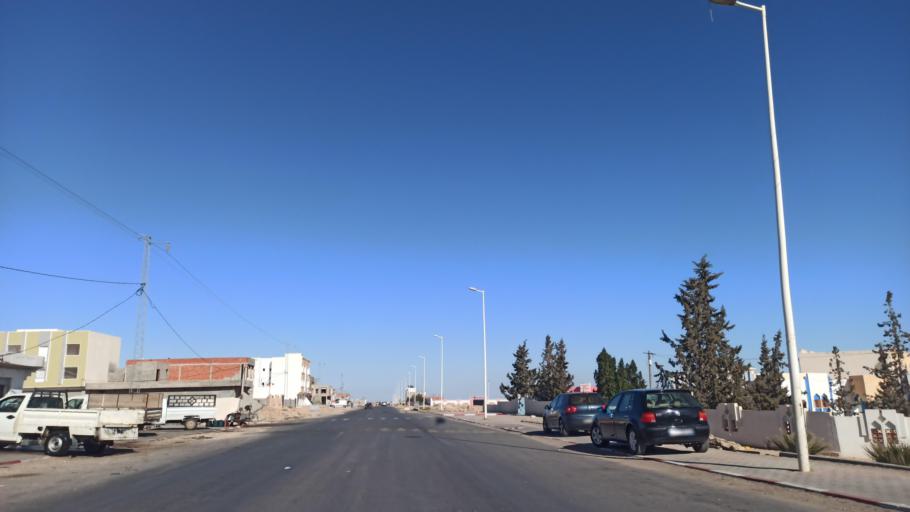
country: TN
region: Sidi Bu Zayd
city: Bi'r al Hufayy
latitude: 34.9407
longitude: 9.2030
